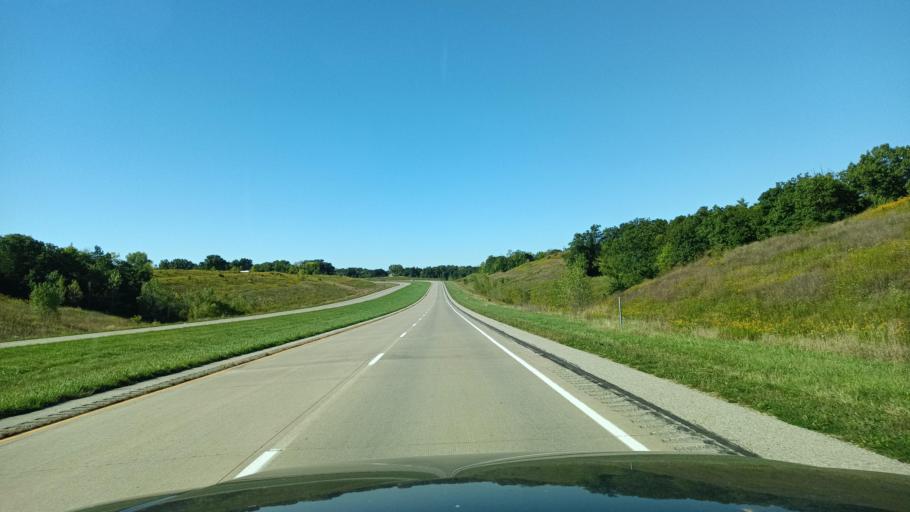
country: US
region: Iowa
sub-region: Lee County
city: Fort Madison
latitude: 40.6467
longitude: -91.3712
